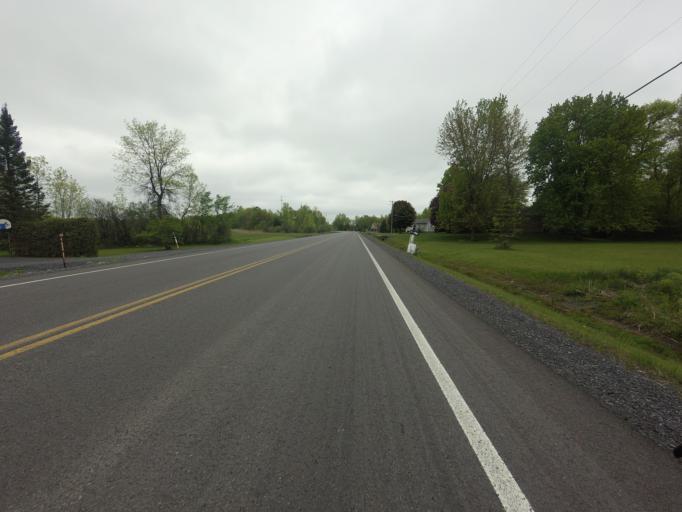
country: US
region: New York
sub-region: St. Lawrence County
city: Norfolk
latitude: 44.9430
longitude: -75.1483
